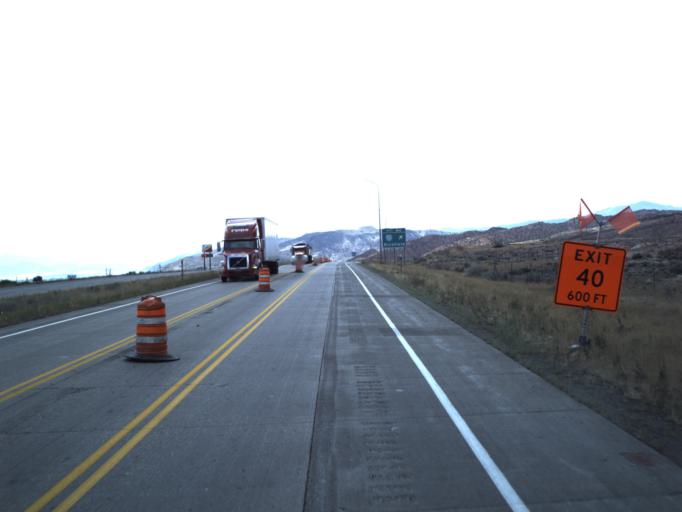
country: US
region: Utah
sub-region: Sevier County
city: Richfield
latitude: 38.7950
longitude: -112.0754
